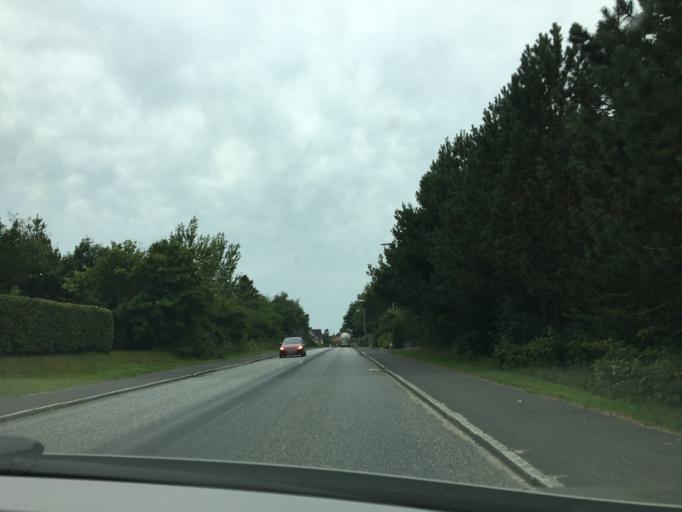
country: DK
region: Central Jutland
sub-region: Viborg Kommune
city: Stoholm
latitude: 56.3926
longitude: 8.9968
